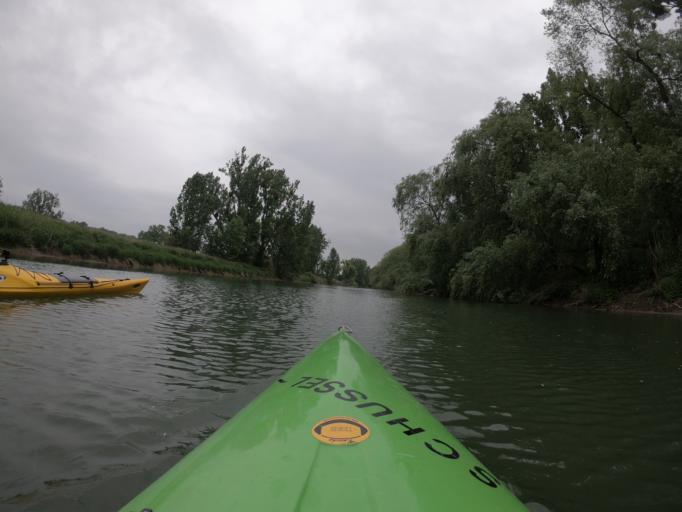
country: DE
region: Hesse
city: Biebesheim
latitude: 49.7985
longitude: 8.4230
